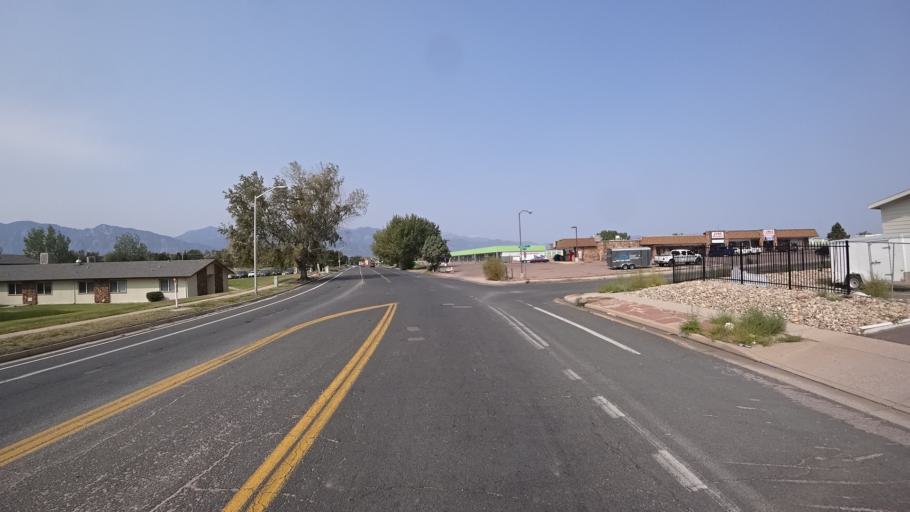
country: US
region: Colorado
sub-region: El Paso County
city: Stratmoor
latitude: 38.8061
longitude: -104.7770
